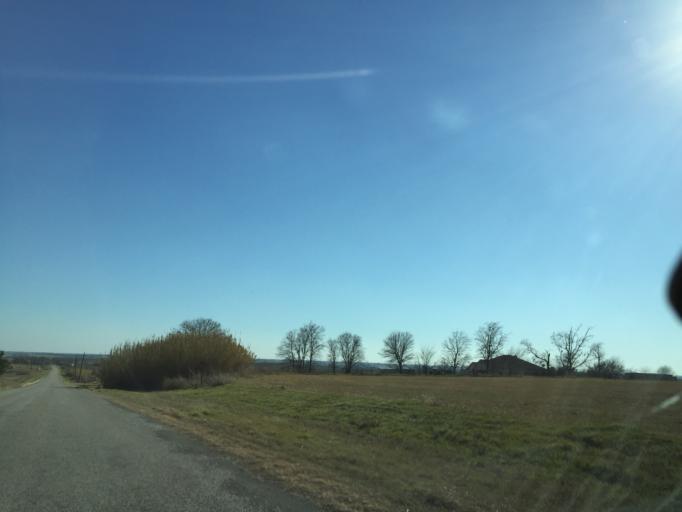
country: US
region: Texas
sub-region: Williamson County
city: Taylor
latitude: 30.5667
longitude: -97.3084
